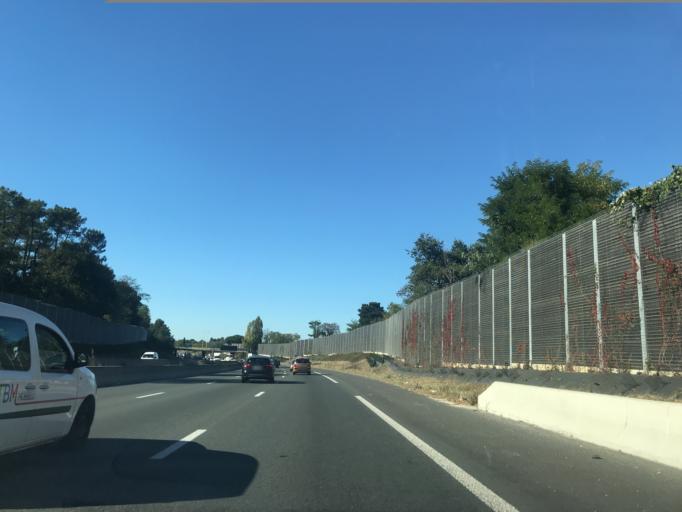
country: FR
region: Aquitaine
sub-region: Departement de la Gironde
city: Pessac
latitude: 44.7982
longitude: -0.6532
